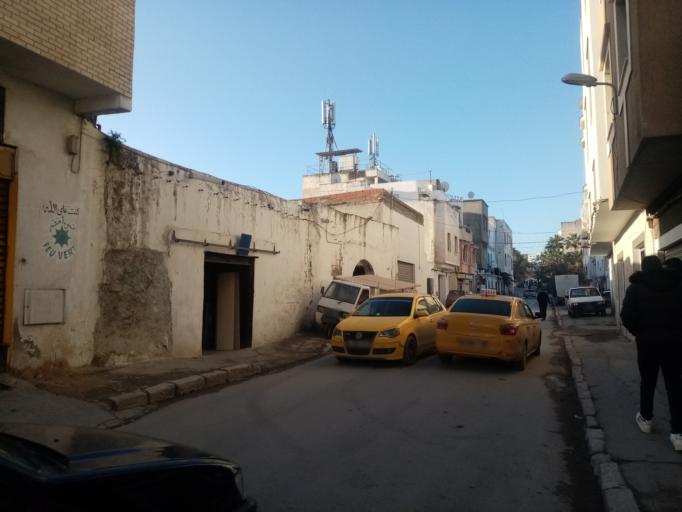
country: TN
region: Tunis
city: Tunis
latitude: 36.7893
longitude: 10.1795
